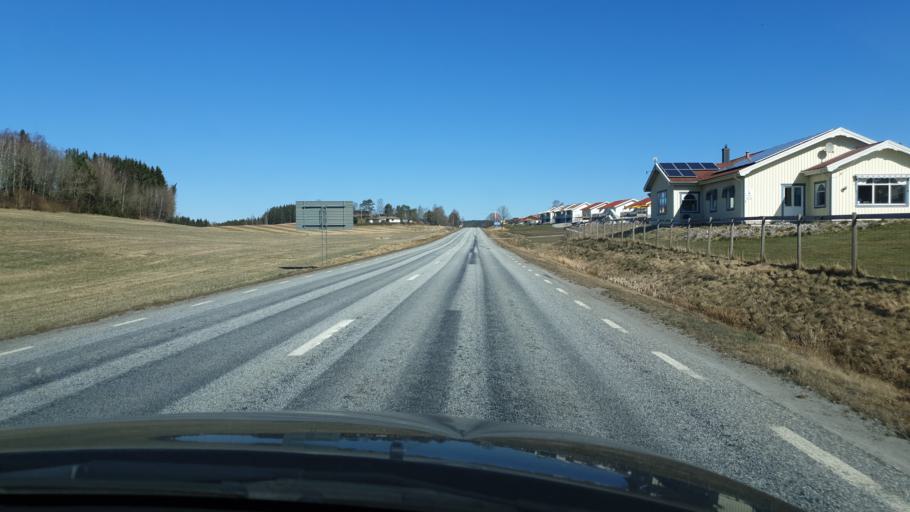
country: SE
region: Vaestra Goetaland
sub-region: Tanums Kommun
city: Tanumshede
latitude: 58.7722
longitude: 11.5575
